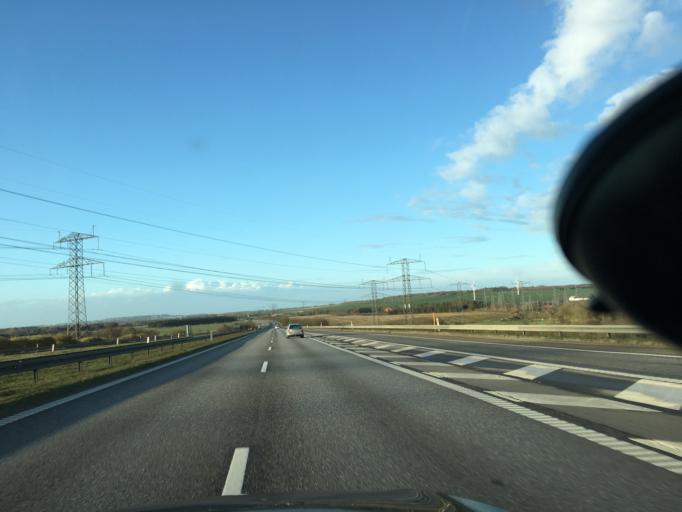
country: DK
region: North Denmark
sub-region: Alborg Kommune
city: Svenstrup
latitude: 56.9513
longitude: 9.8667
